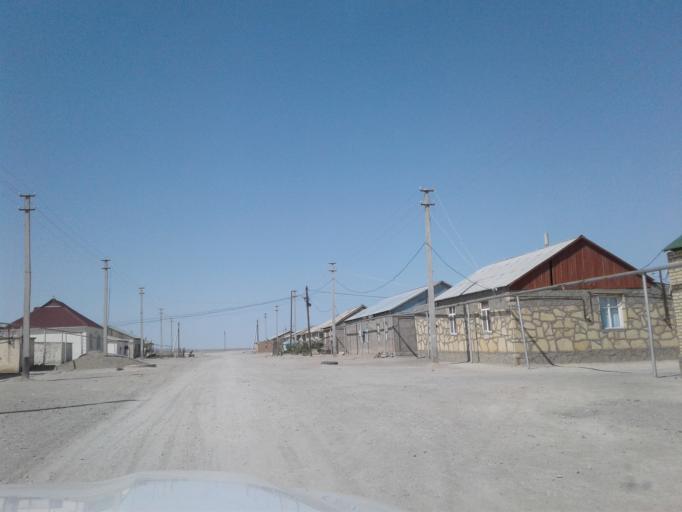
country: TM
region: Balkan
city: Gazanjyk
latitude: 39.1513
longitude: 55.3106
